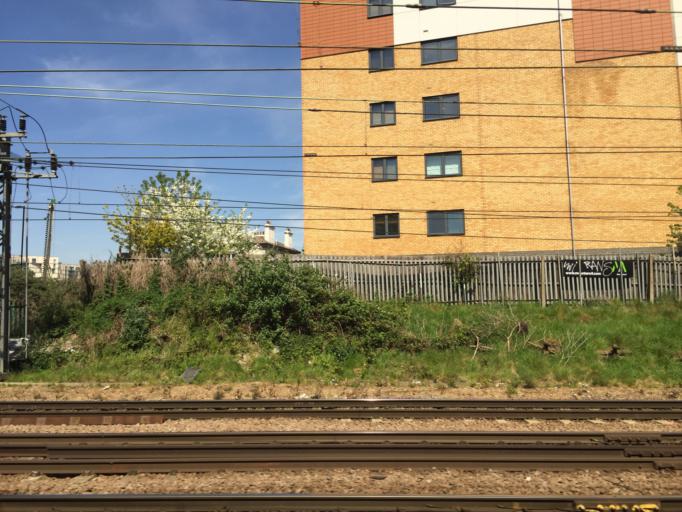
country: GB
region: England
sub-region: Greater London
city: Poplar
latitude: 51.5447
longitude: 0.0012
